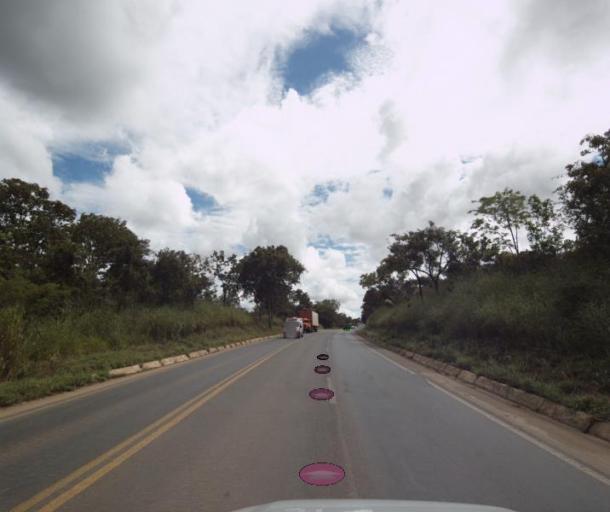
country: BR
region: Goias
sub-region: Uruacu
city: Uruacu
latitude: -14.4895
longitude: -49.1533
